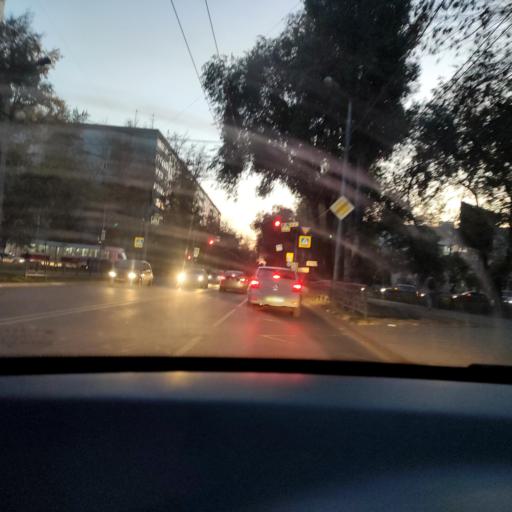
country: RU
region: Samara
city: Samara
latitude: 53.1997
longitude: 50.1390
